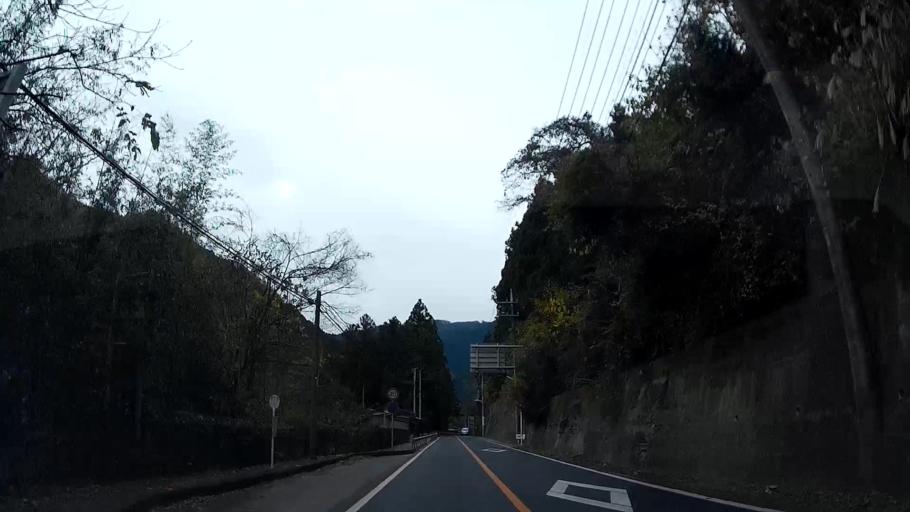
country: JP
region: Saitama
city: Chichibu
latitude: 35.9612
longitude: 138.9738
